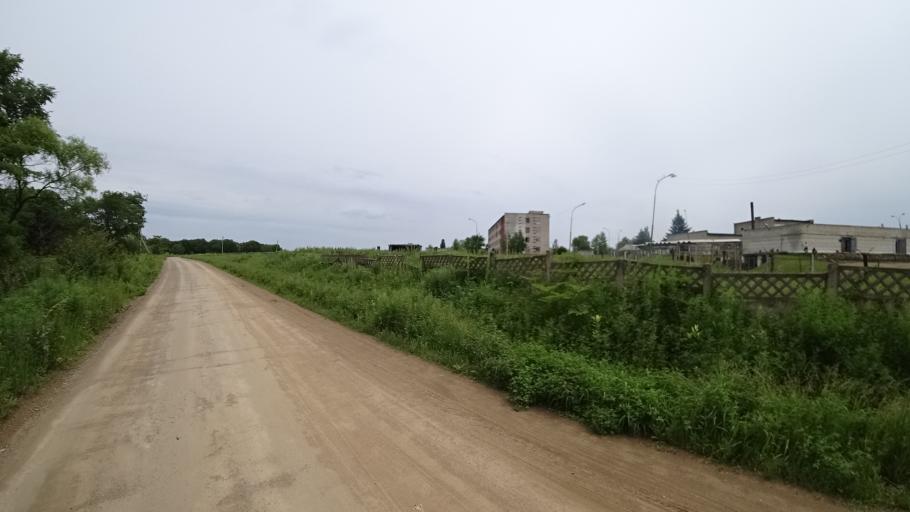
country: RU
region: Primorskiy
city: Arsen'yev
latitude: 44.1996
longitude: 133.3100
